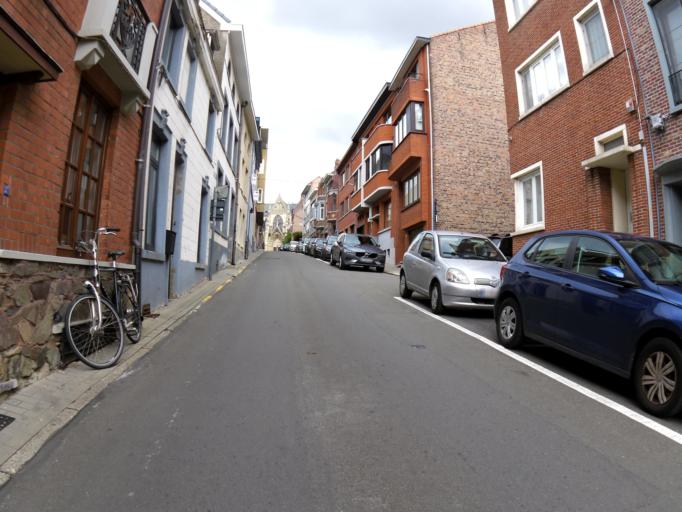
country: BE
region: Flanders
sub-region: Provincie Limburg
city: Tongeren
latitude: 50.7793
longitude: 5.4668
